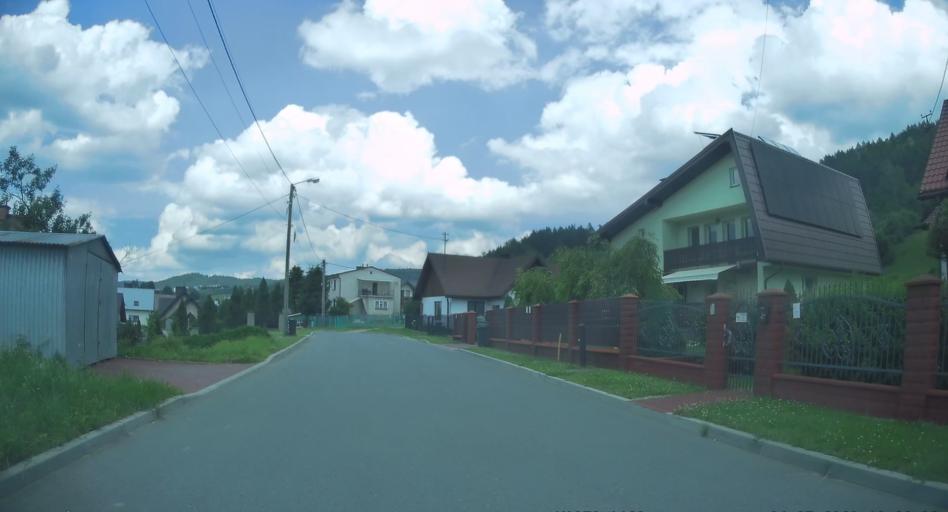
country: PL
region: Lesser Poland Voivodeship
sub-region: Powiat nowosadecki
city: Krynica-Zdroj
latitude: 49.3870
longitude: 20.9536
